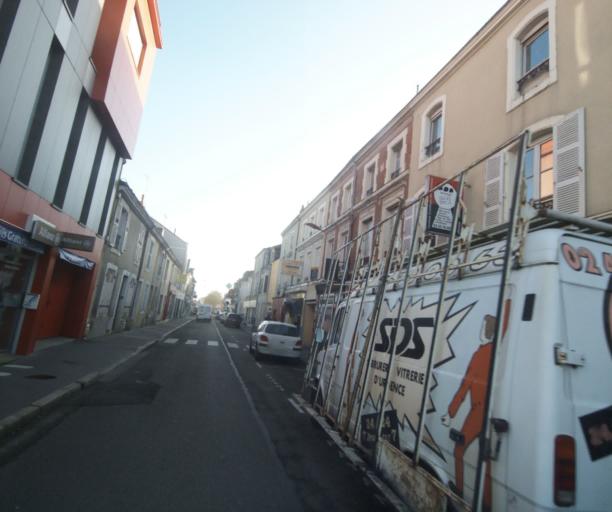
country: FR
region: Pays de la Loire
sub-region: Departement de la Sarthe
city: Le Mans
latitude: 47.9967
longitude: 0.2016
